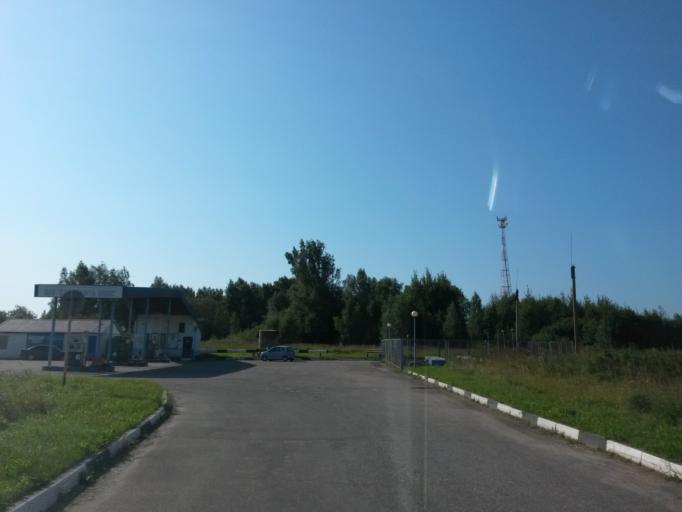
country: RU
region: Jaroslavl
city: Gavrilov-Yam
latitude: 57.3096
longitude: 39.9381
